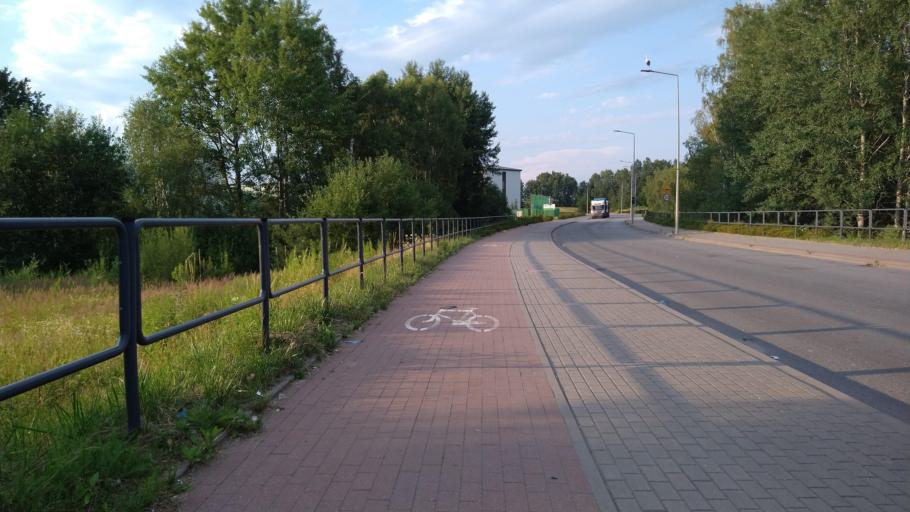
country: PL
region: Warmian-Masurian Voivodeship
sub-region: Powiat olsztynski
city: Olsztyn
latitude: 53.7859
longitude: 20.5519
